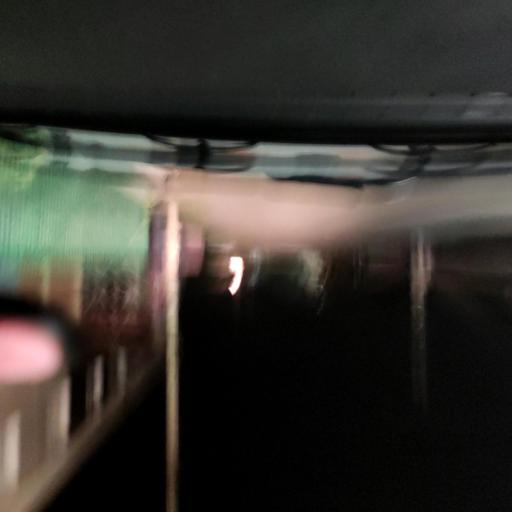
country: RU
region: Voronezj
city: Novaya Usman'
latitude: 51.6366
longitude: 39.4241
